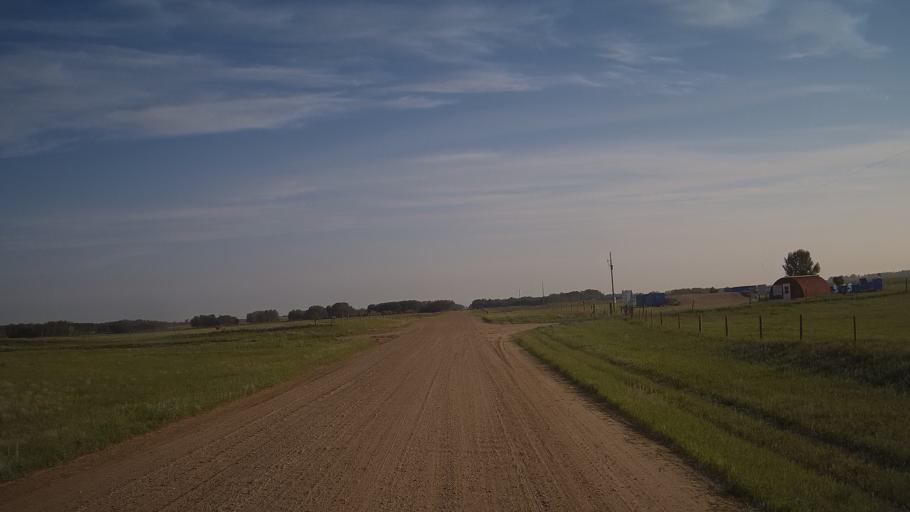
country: CA
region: Saskatchewan
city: Saskatoon
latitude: 51.8231
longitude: -106.5238
